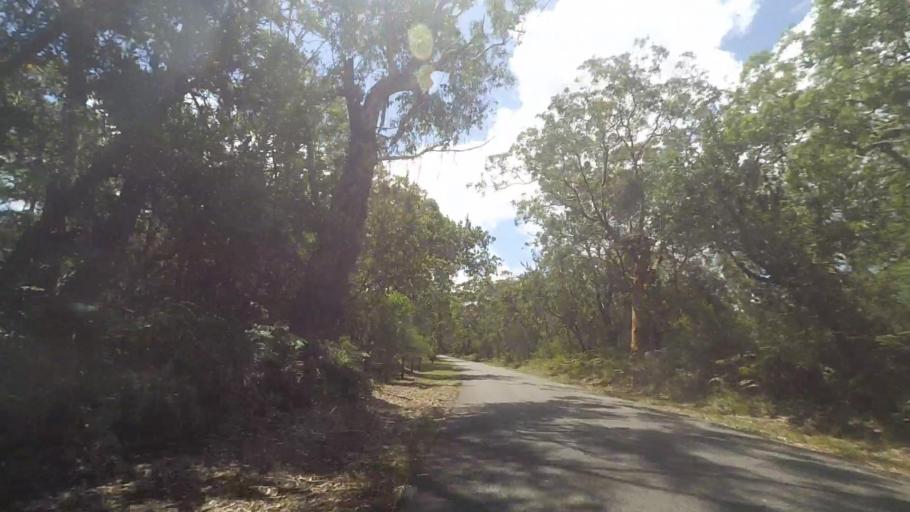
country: AU
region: New South Wales
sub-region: Great Lakes
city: Bulahdelah
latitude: -32.5077
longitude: 152.3171
